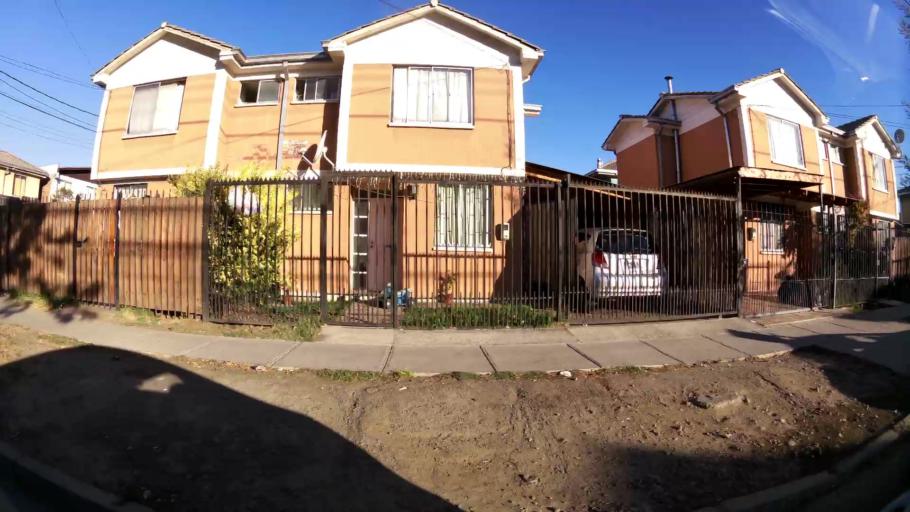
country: CL
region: O'Higgins
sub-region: Provincia de Cachapoal
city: Rancagua
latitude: -34.1757
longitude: -70.7605
